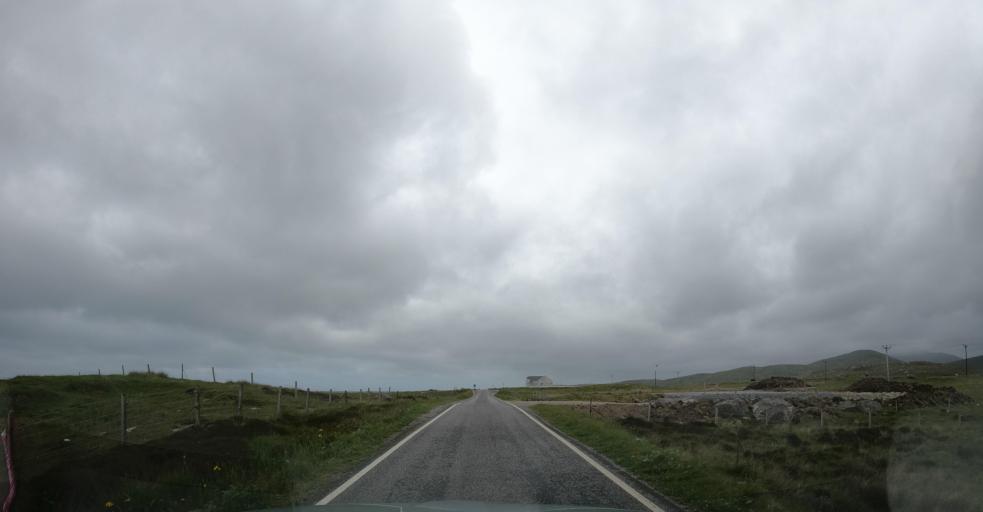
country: GB
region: Scotland
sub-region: Eilean Siar
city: Isle of South Uist
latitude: 57.1979
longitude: -7.3902
